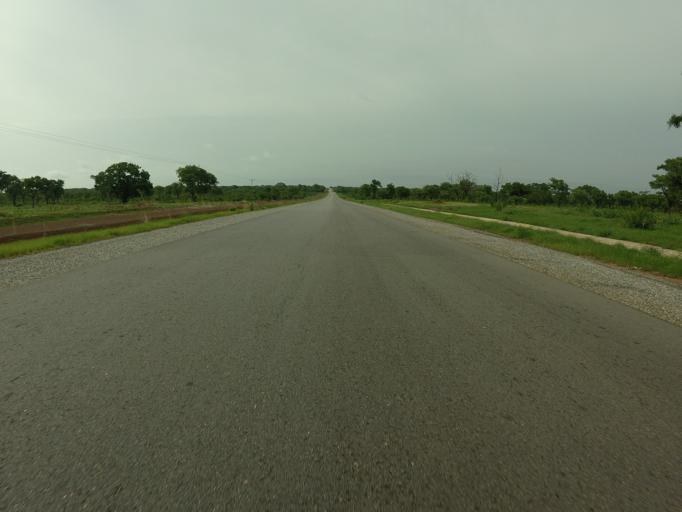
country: GH
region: Northern
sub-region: Yendi
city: Yendi
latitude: 9.6306
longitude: -0.0584
